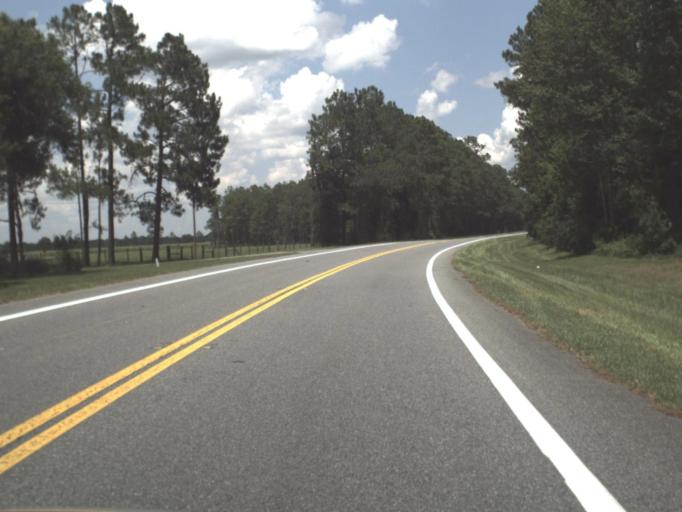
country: US
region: Florida
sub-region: Union County
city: Lake Butler
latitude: 30.1130
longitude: -82.2159
